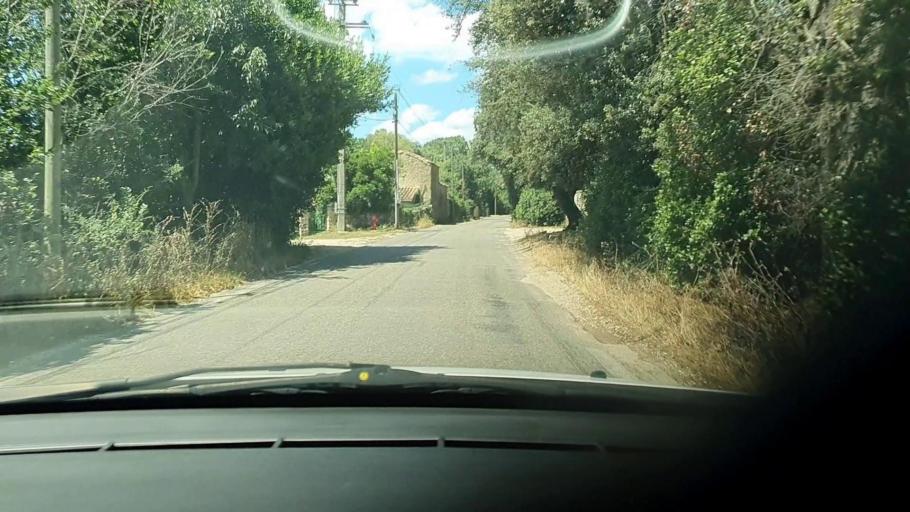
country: FR
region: Languedoc-Roussillon
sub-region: Departement du Gard
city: Uzes
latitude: 44.0045
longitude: 4.3927
